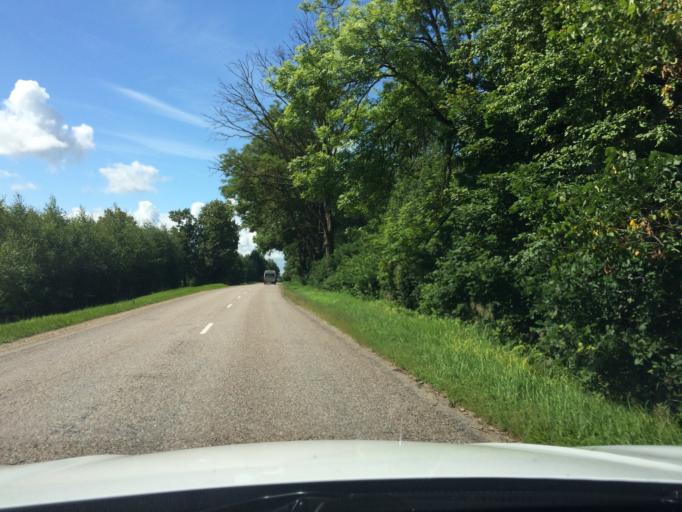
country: LV
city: Tervete
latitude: 56.5177
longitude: 23.4887
